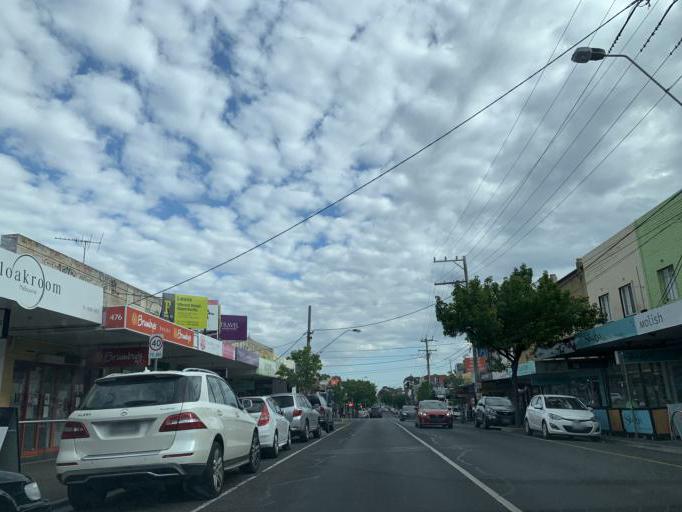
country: AU
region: Victoria
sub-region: Bayside
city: Hampton
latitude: -37.9357
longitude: 145.0028
